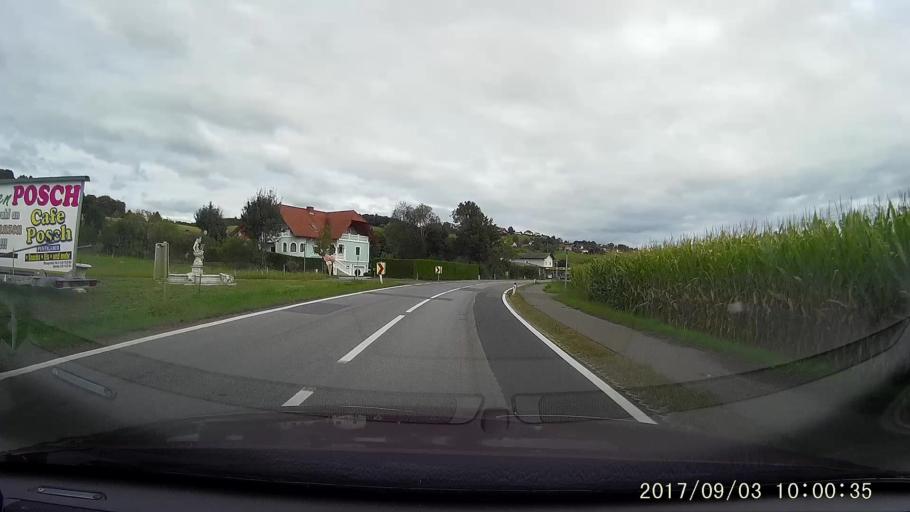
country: AT
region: Styria
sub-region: Politischer Bezirk Suedoststeiermark
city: Muehldorf bei Feldbach
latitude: 46.9291
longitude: 15.8900
